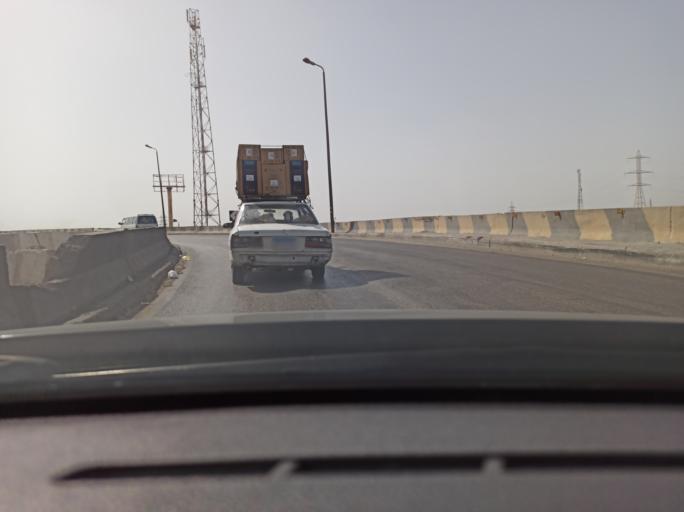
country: EG
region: Muhafazat al Qahirah
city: Halwan
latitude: 29.7904
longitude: 31.3455
